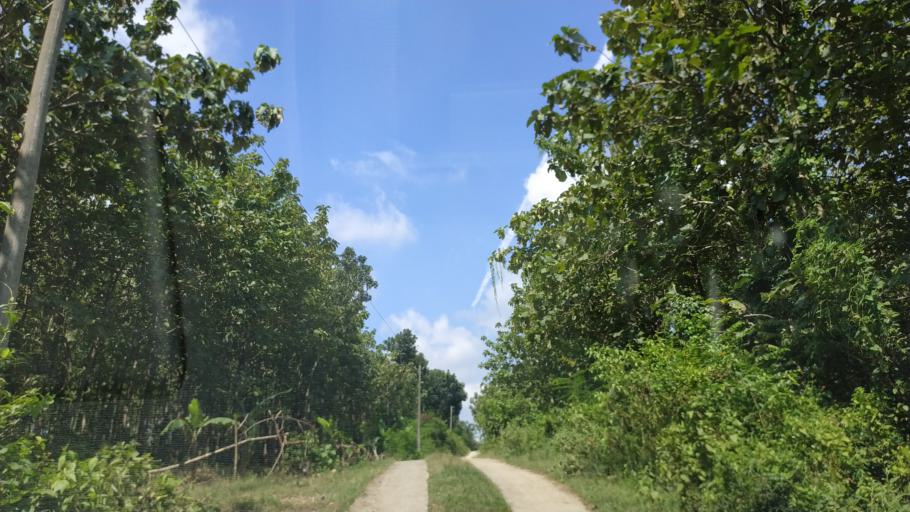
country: ID
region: Central Java
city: Guyangan
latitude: -7.0050
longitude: 111.0943
